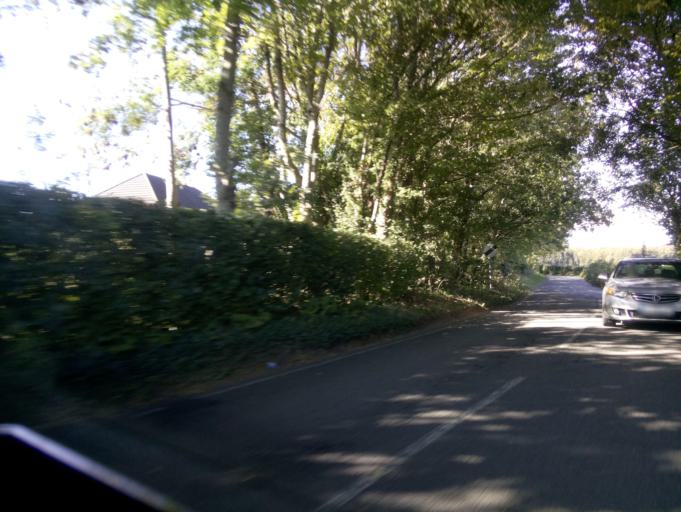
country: GB
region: Wales
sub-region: Newport
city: Newport
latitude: 51.5955
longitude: -3.0445
